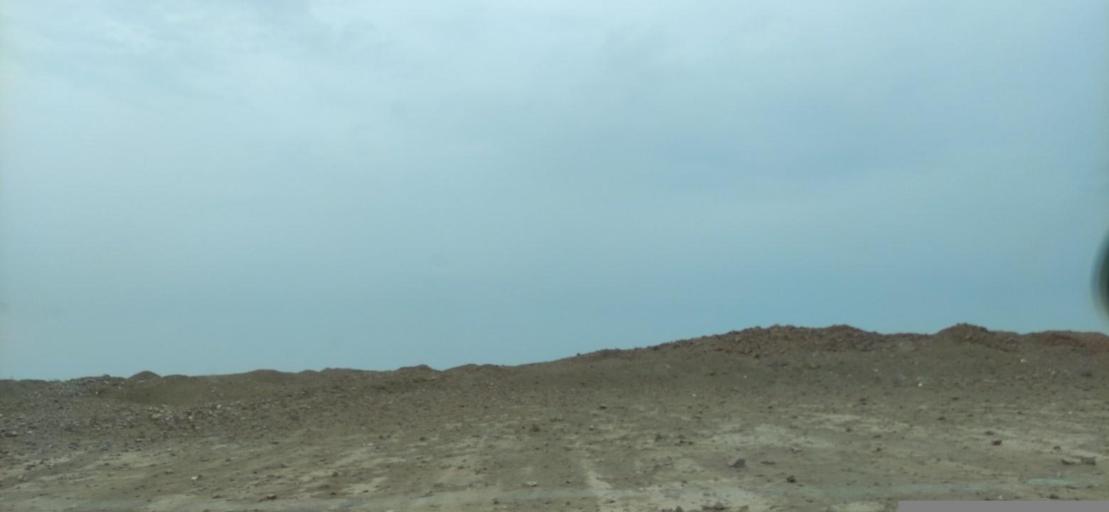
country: KZ
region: Qaraghandy
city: Saryshaghan
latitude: 46.1244
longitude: 73.5961
